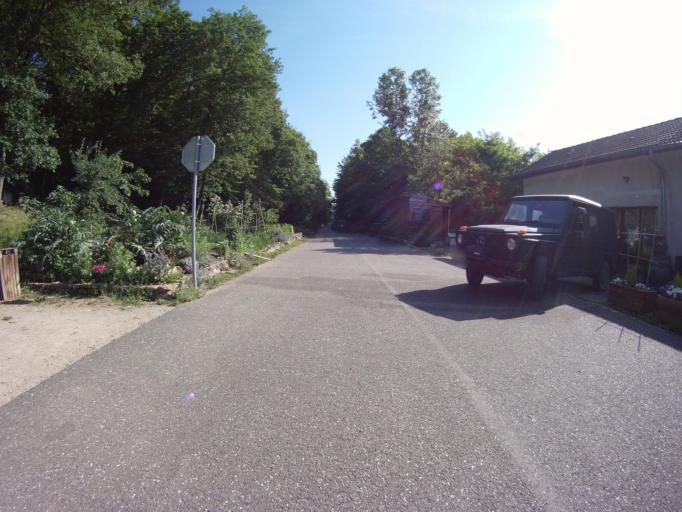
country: FR
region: Lorraine
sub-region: Departement de Meurthe-et-Moselle
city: Champenoux
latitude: 48.7413
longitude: 6.3157
